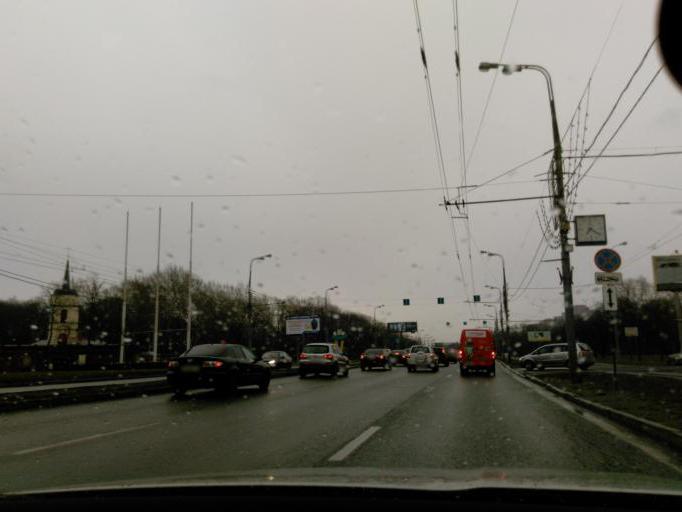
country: RU
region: Moscow
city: Pokrovskoye-Streshnevo
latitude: 55.8144
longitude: 37.4695
